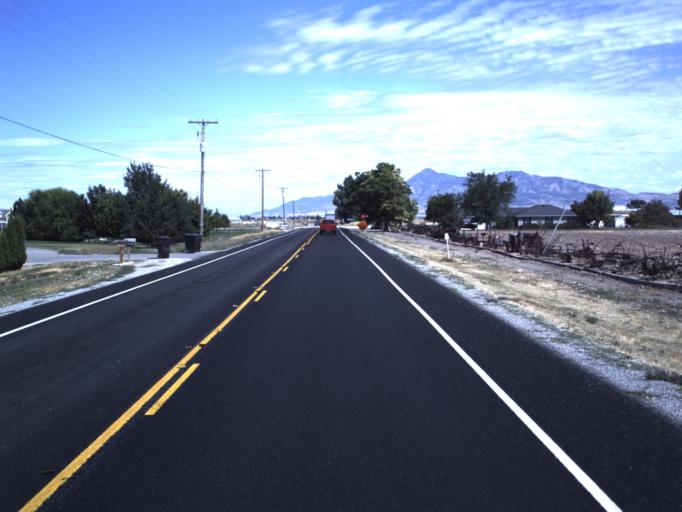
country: US
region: Utah
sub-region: Box Elder County
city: Garland
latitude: 41.7355
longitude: -112.1433
